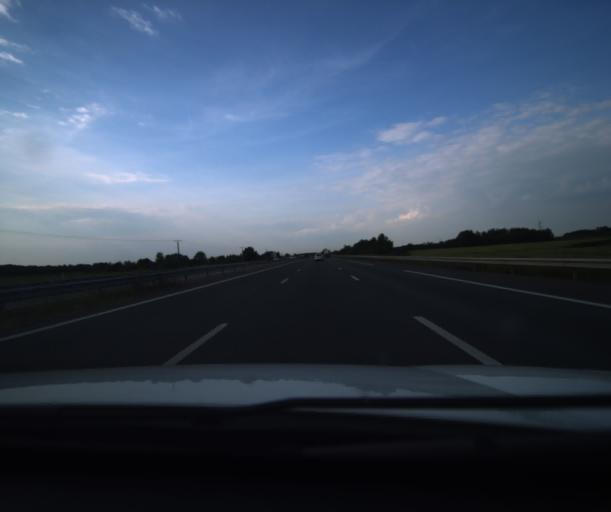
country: FR
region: Midi-Pyrenees
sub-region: Departement du Tarn-et-Garonne
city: Campsas
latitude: 43.8606
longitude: 1.3186
